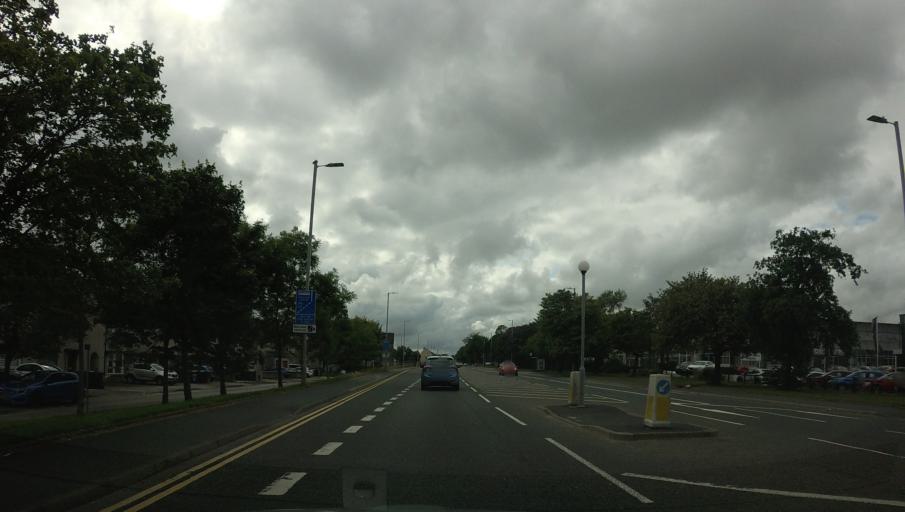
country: GB
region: Scotland
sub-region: Aberdeen City
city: Cults
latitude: 57.1514
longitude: -2.1585
